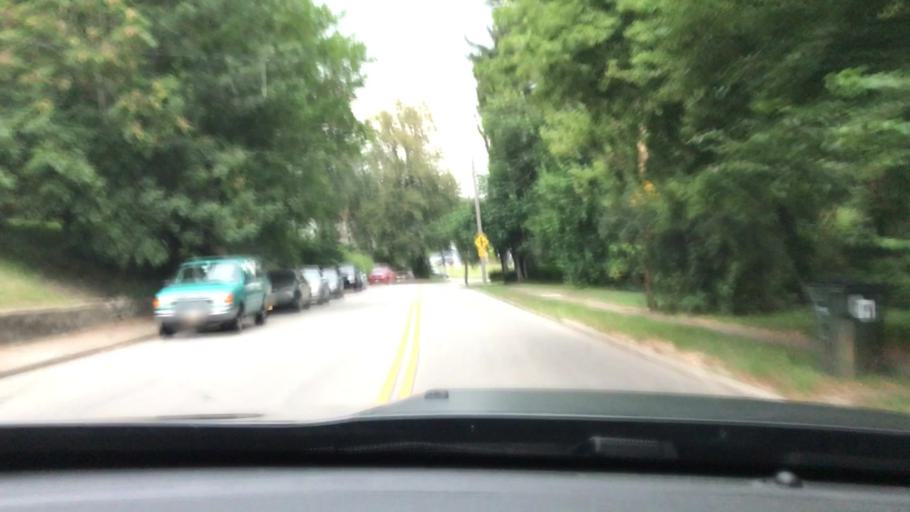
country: US
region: Iowa
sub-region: Scott County
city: Bettendorf
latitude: 41.5346
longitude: -90.5423
